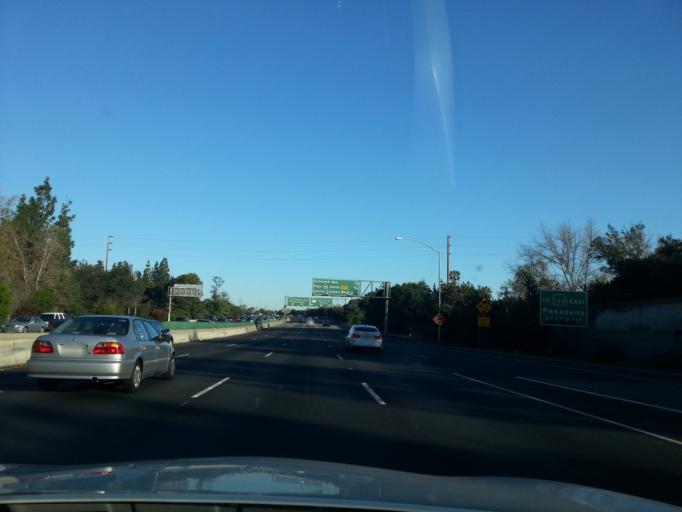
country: US
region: California
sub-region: Los Angeles County
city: Universal City
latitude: 34.1424
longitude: -118.3669
